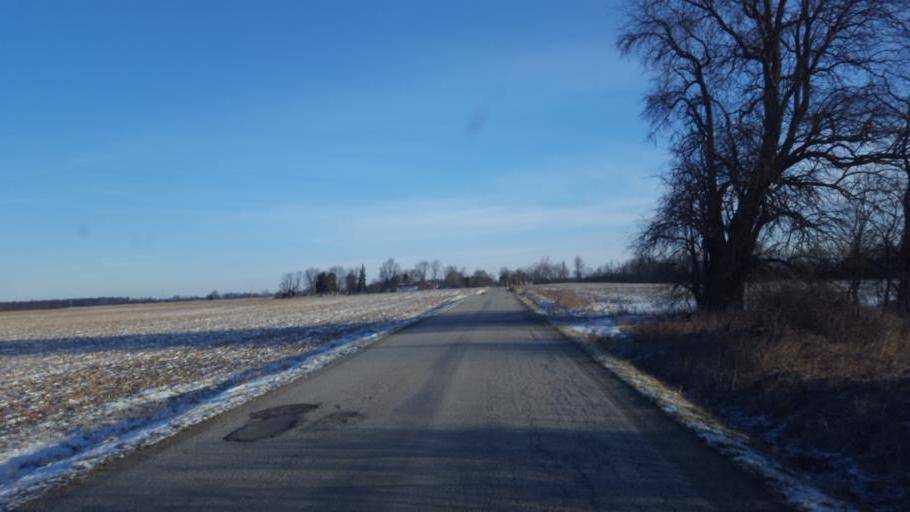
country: US
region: Ohio
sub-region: Morrow County
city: Cardington
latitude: 40.5317
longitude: -82.9194
